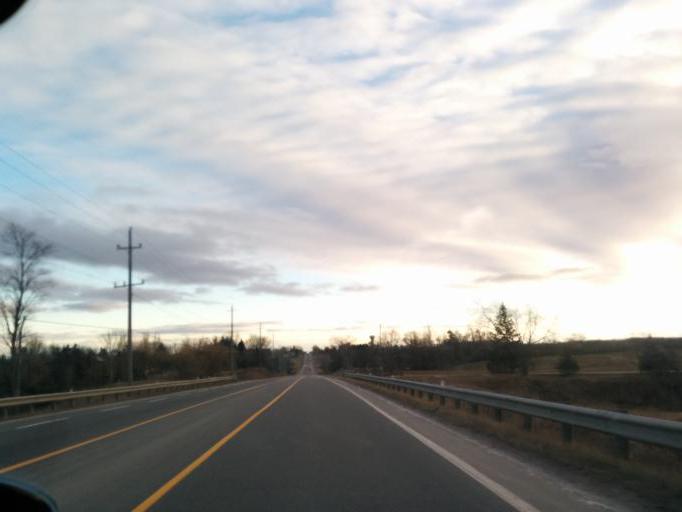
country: CA
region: Ontario
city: Bradford West Gwillimbury
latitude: 43.9342
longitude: -79.6604
